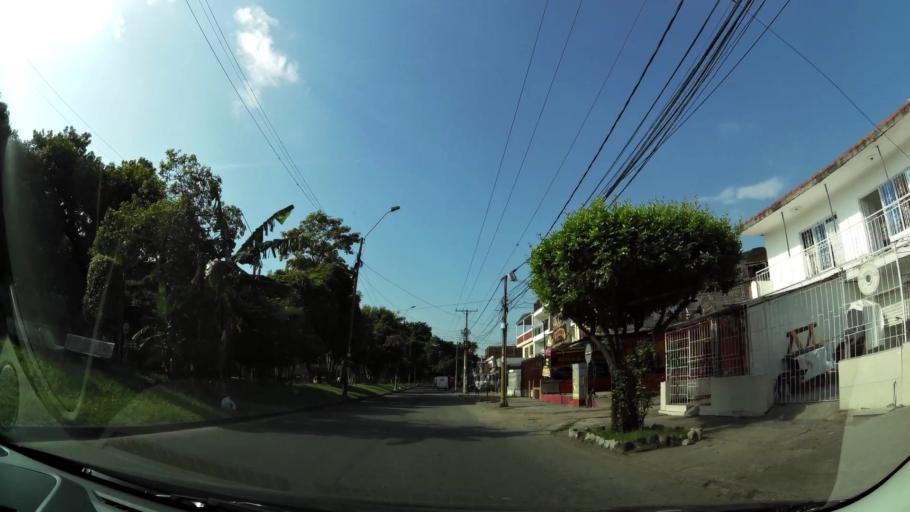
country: CO
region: Valle del Cauca
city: Cali
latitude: 3.4169
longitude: -76.5278
